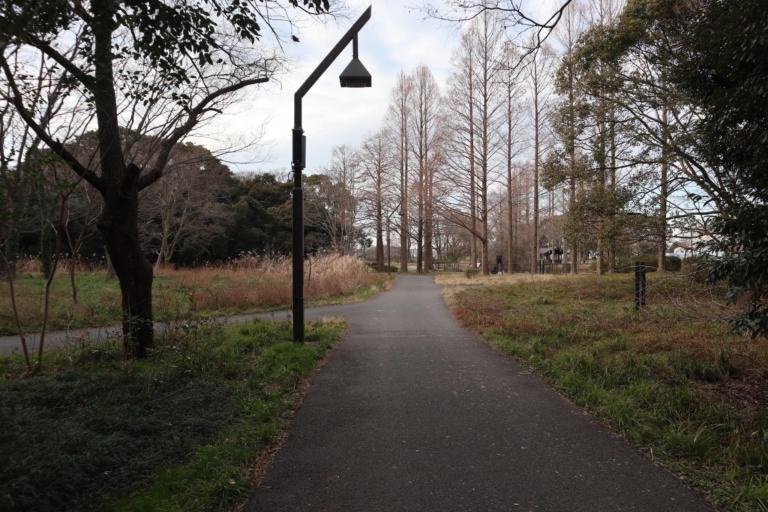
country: JP
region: Chiba
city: Matsudo
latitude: 35.7950
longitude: 139.8739
